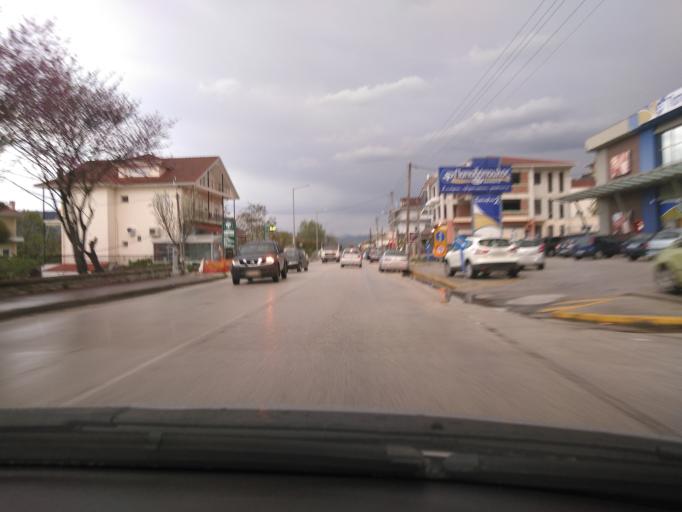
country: GR
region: Epirus
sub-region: Nomos Ioanninon
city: Katsikas
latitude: 39.6298
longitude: 20.8791
